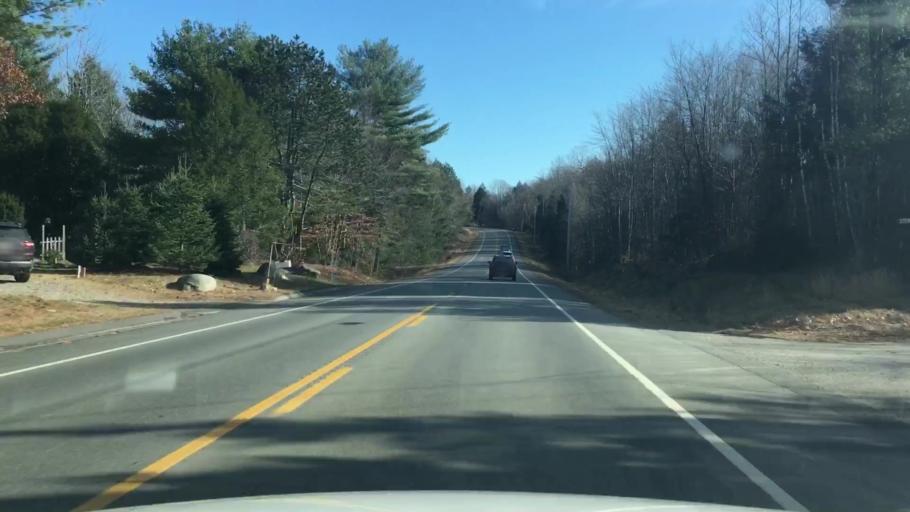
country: US
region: Maine
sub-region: Knox County
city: Washington
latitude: 44.2478
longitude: -69.4008
